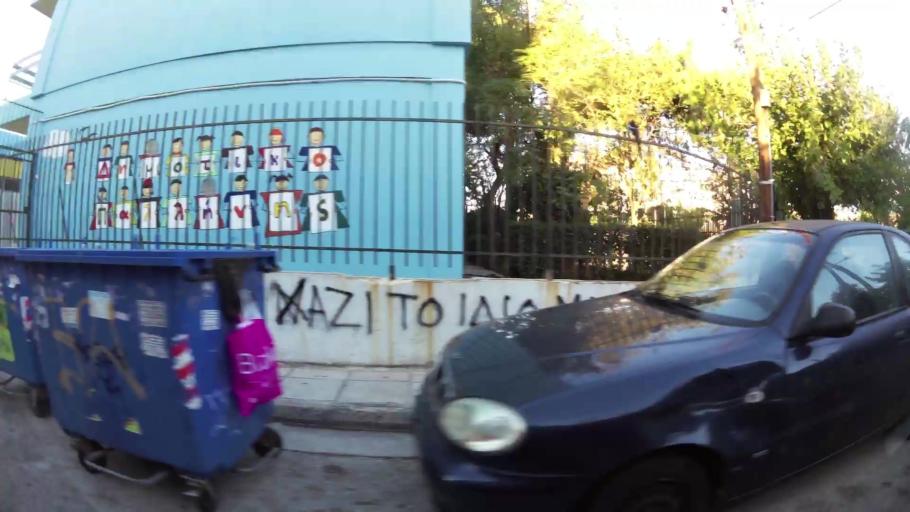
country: GR
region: Attica
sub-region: Nomarchia Anatolikis Attikis
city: Pallini
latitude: 38.0015
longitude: 23.8812
